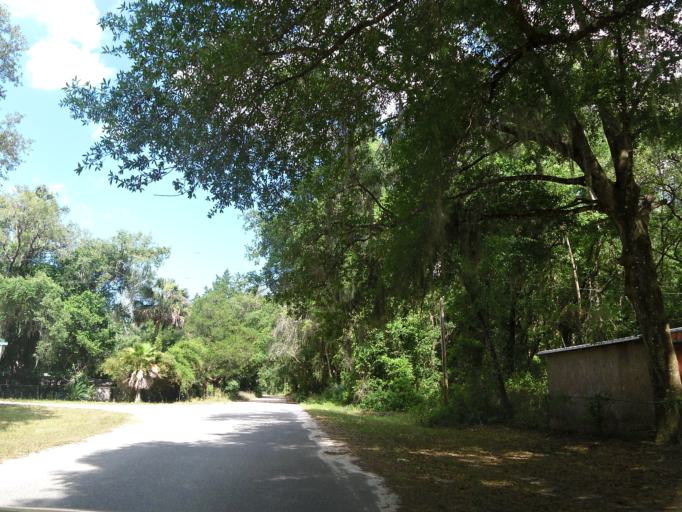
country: US
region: Florida
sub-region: Putnam County
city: Interlachen
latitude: 29.7317
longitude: -81.8853
